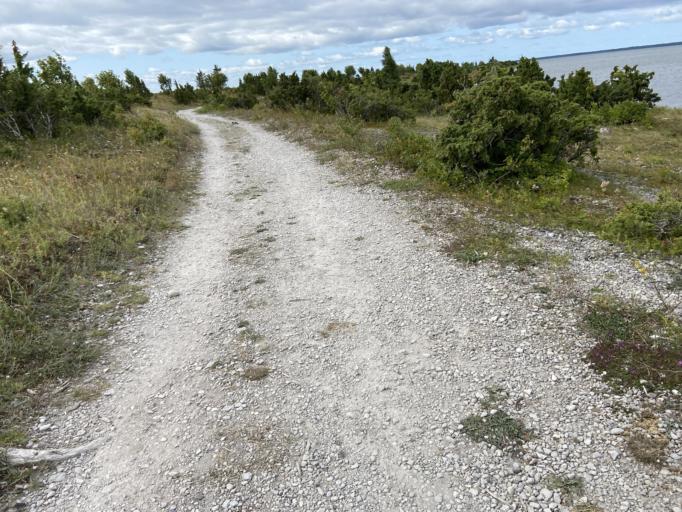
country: EE
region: Hiiumaa
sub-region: Kaerdla linn
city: Kardla
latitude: 58.7633
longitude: 22.8060
